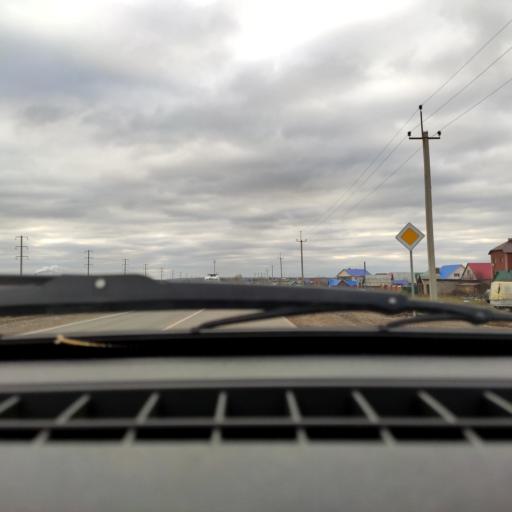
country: RU
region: Bashkortostan
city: Iglino
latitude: 54.7905
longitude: 56.2517
